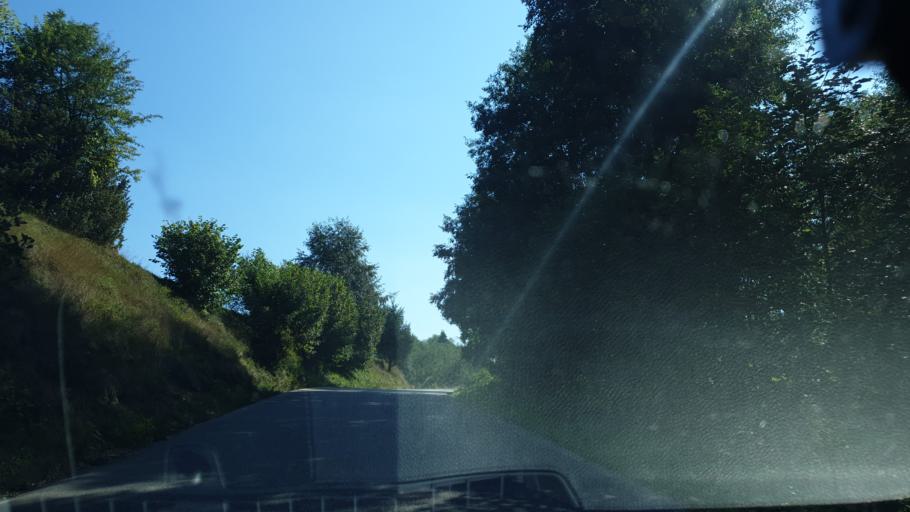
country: RS
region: Central Serbia
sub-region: Zlatiborski Okrug
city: Nova Varos
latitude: 43.4383
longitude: 19.8597
